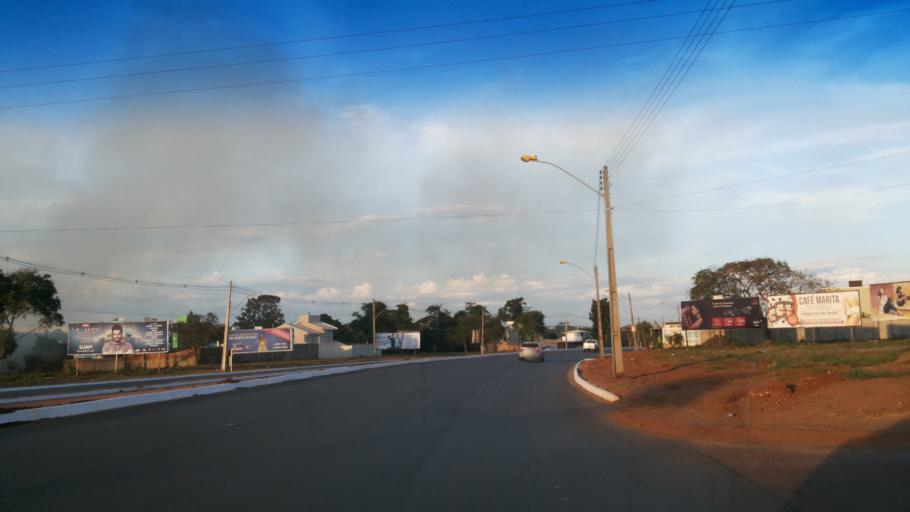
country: BR
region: Goias
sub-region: Goiania
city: Goiania
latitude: -16.6230
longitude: -49.2776
